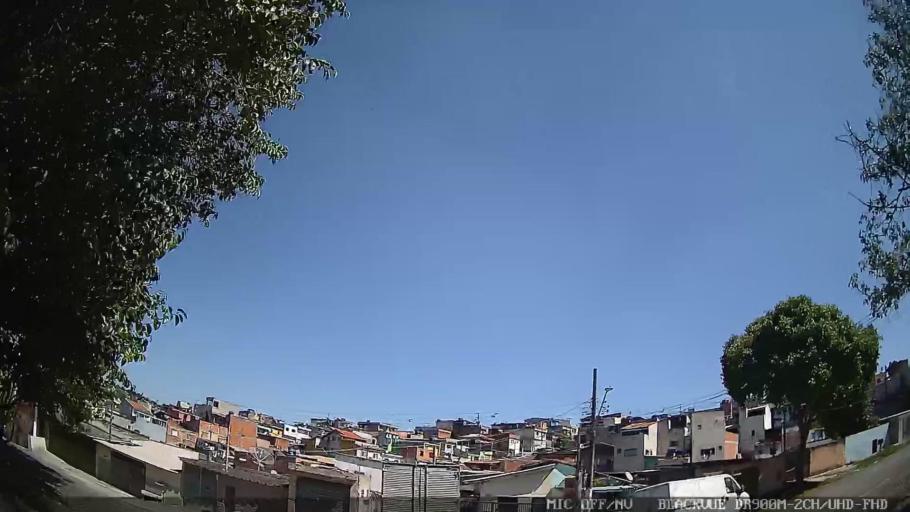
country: BR
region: Sao Paulo
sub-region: Sao Caetano Do Sul
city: Sao Caetano do Sul
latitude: -23.5913
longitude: -46.4977
